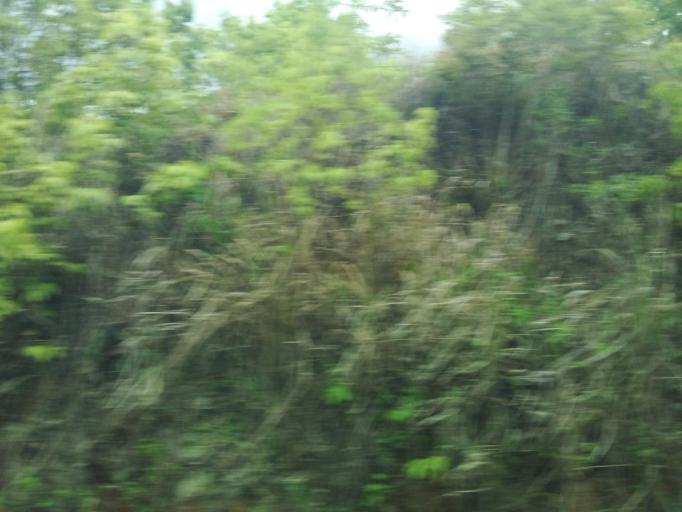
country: BR
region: Minas Gerais
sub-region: Nova Era
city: Nova Era
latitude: -19.6661
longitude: -42.8904
